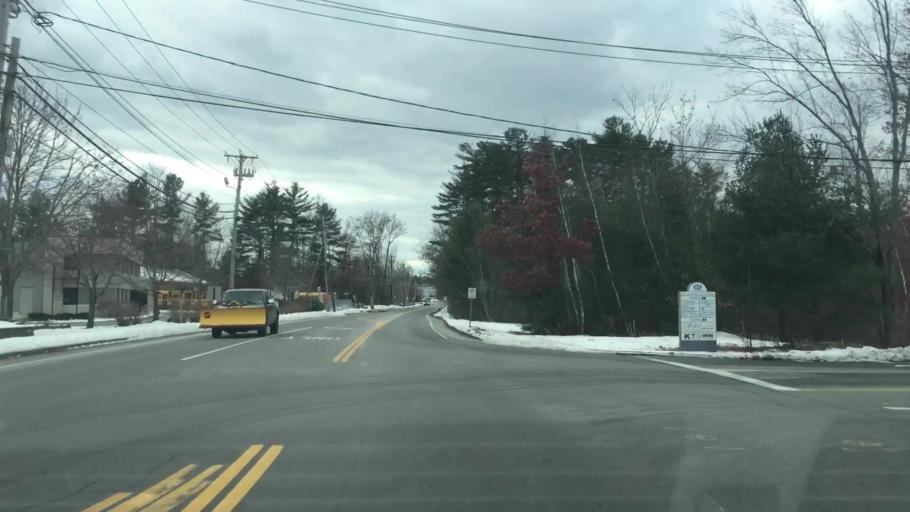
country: US
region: New Hampshire
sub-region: Rockingham County
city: Salem
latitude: 42.7653
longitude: -71.2406
